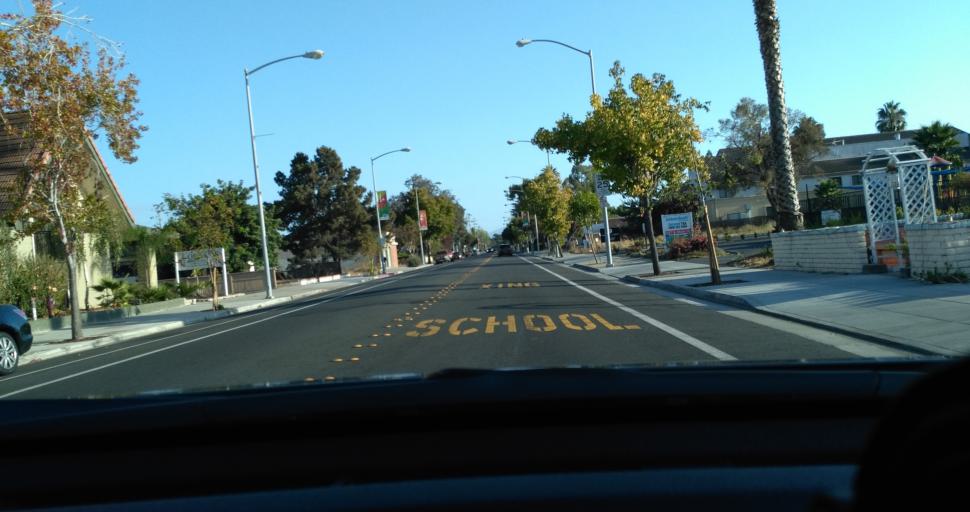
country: US
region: California
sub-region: Santa Clara County
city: Milpitas
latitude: 37.4277
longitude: -121.9062
